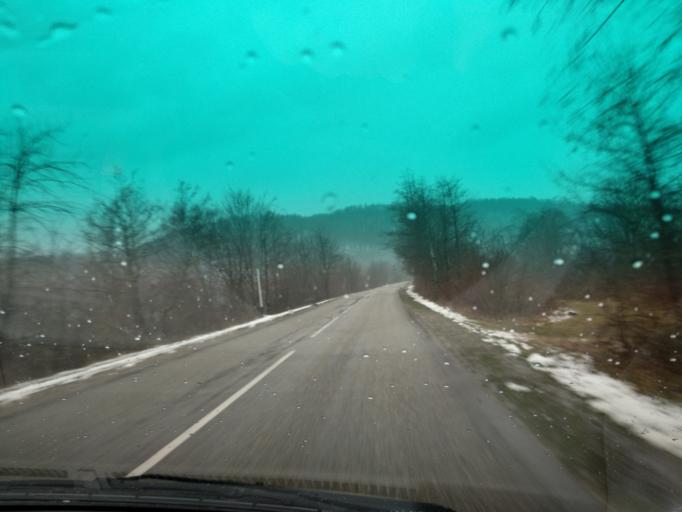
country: RU
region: Krasnodarskiy
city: Khadyzhensk
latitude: 44.2331
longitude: 39.3813
